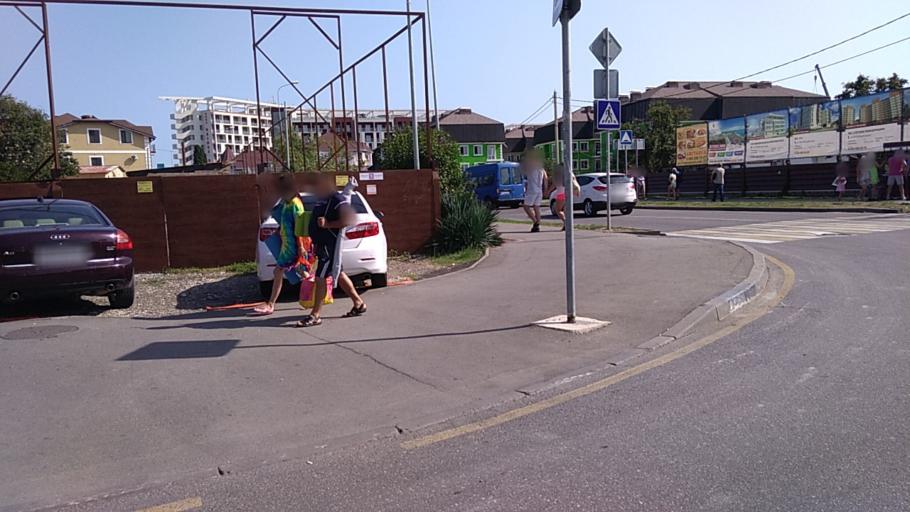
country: RU
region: Krasnodarskiy
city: Adler
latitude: 43.3920
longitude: 39.9867
